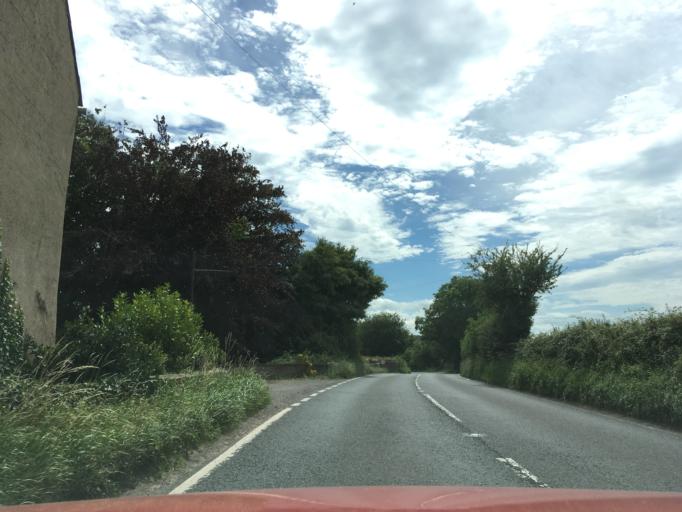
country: GB
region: England
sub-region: Somerset
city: Glastonbury
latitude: 51.1778
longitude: -2.6928
